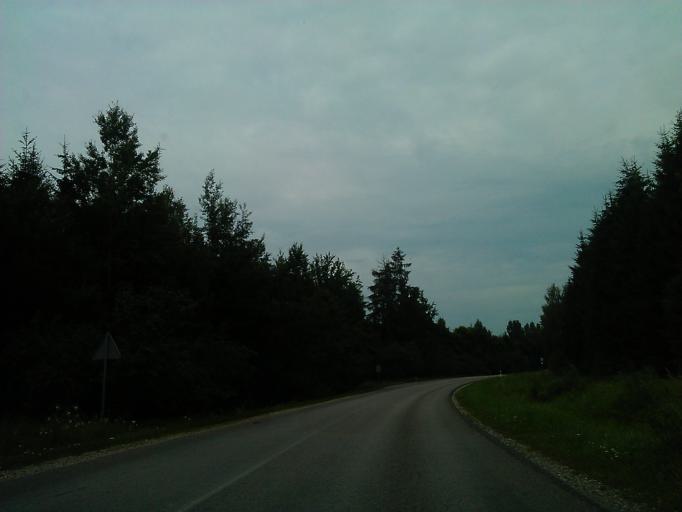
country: LV
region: Beverina
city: Murmuiza
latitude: 57.4409
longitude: 25.4376
